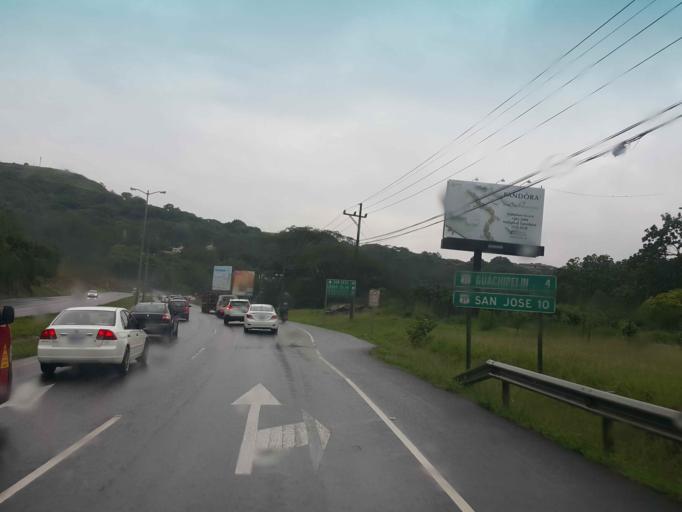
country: CR
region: San Jose
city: Santa Ana
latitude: 9.9465
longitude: -84.1800
